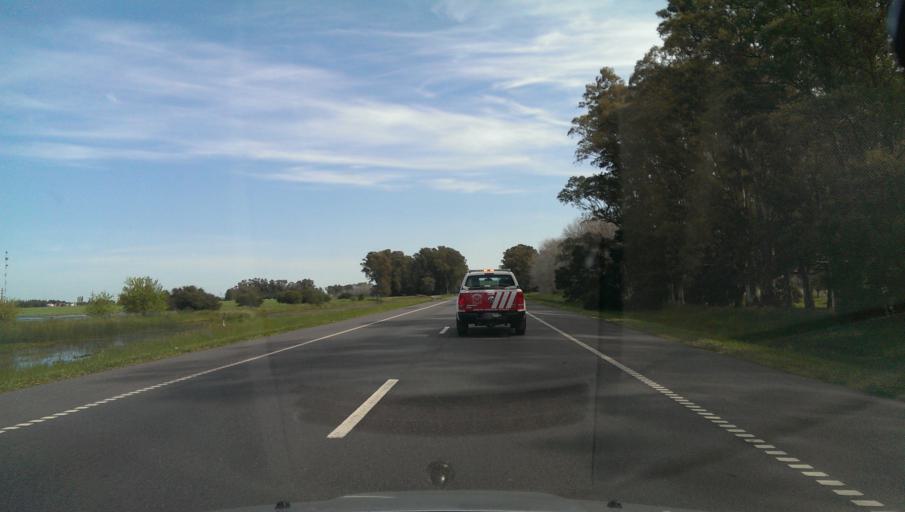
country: AR
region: Buenos Aires
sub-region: Partido de Las Flores
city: Las Flores
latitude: -36.3802
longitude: -59.4827
